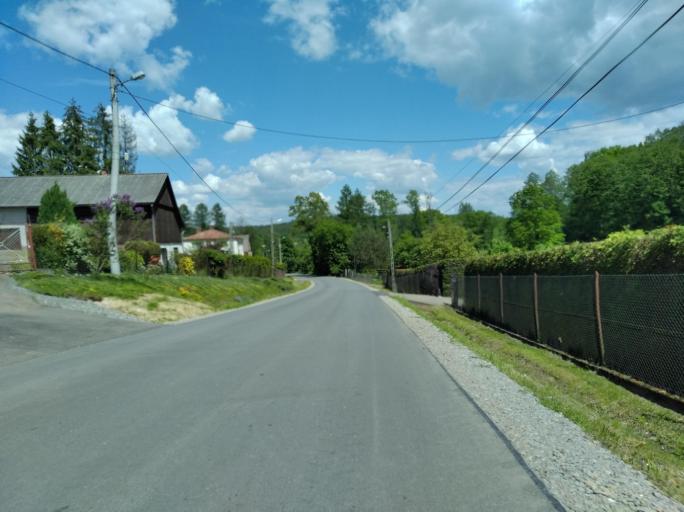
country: PL
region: Subcarpathian Voivodeship
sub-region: Powiat krosnienski
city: Leki
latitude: 49.7793
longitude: 21.6117
